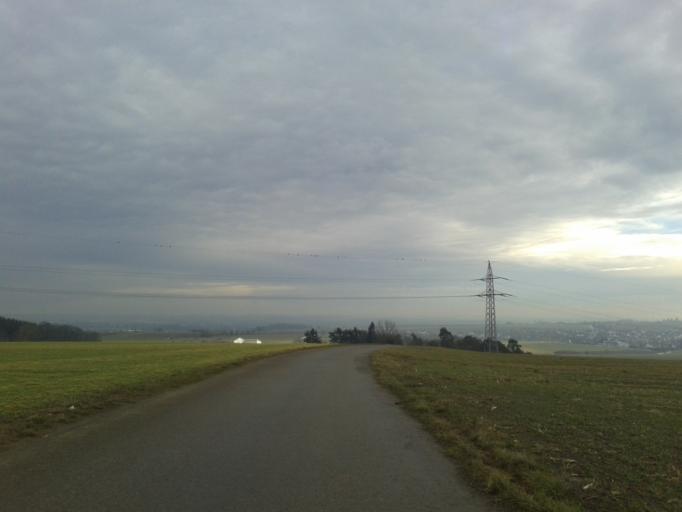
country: DE
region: Baden-Wuerttemberg
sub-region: Tuebingen Region
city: Erbach
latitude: 48.3681
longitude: 9.8965
